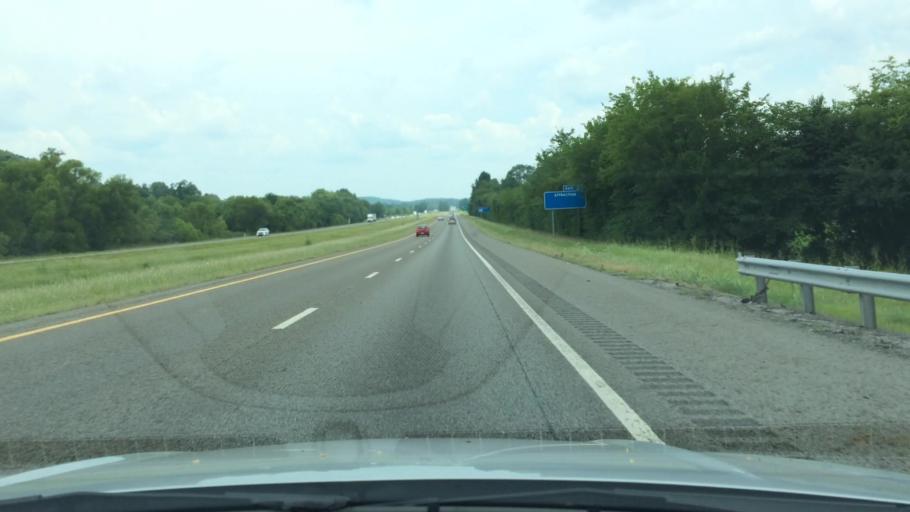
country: US
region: Tennessee
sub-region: Marshall County
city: Cornersville
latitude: 35.4280
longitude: -86.8791
